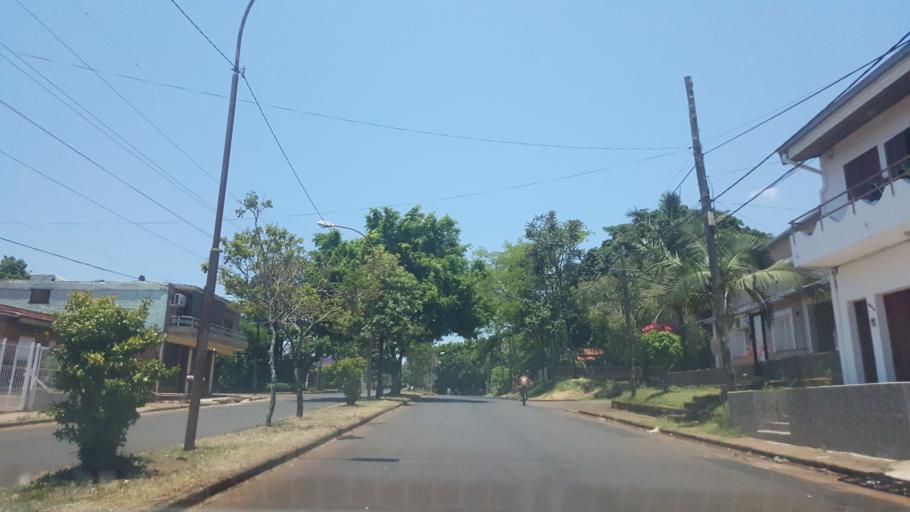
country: AR
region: Misiones
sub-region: Departamento de Capital
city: Posadas
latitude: -27.3963
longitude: -55.8940
